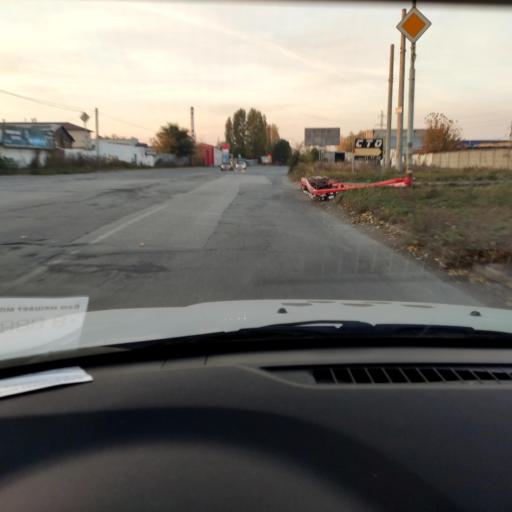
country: RU
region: Samara
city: Tol'yatti
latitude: 53.5225
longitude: 49.4697
